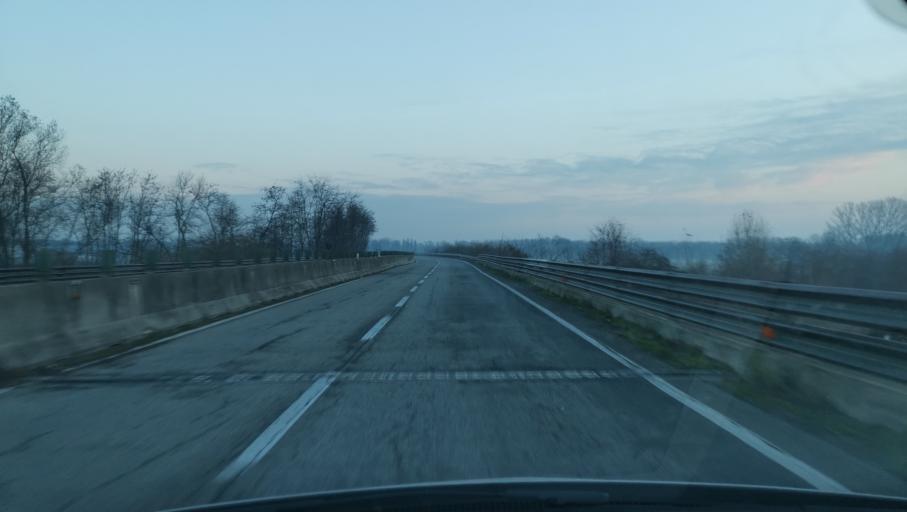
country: IT
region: Piedmont
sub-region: Provincia di Torino
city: Brandizzo
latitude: 45.1792
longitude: 7.8568
